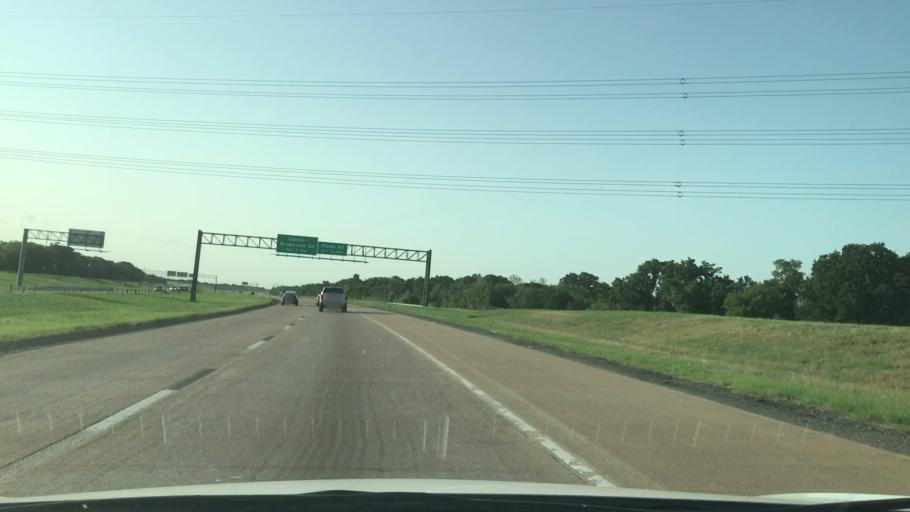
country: US
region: Texas
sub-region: Tarrant County
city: Euless
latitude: 32.8694
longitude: -97.0663
